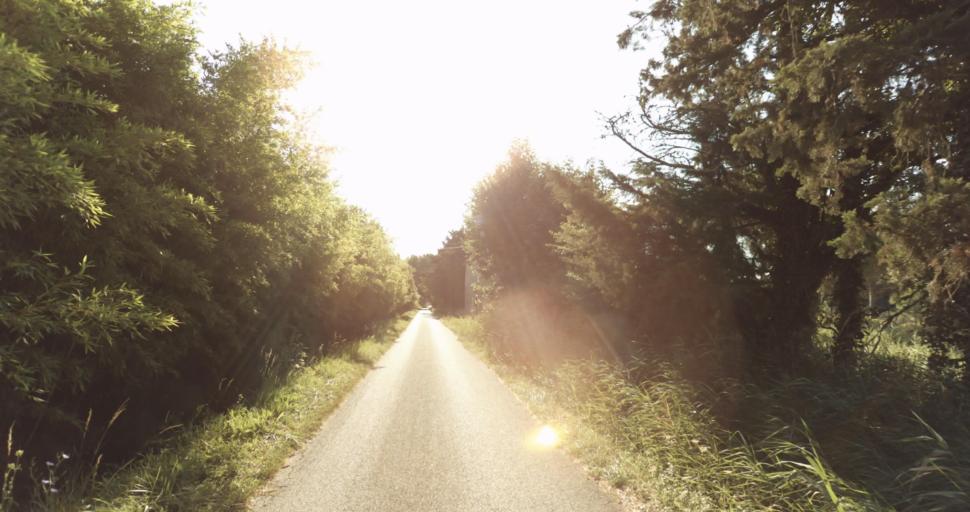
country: FR
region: Provence-Alpes-Cote d'Azur
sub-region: Departement du Vaucluse
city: Althen-des-Paluds
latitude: 44.0435
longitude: 4.9587
